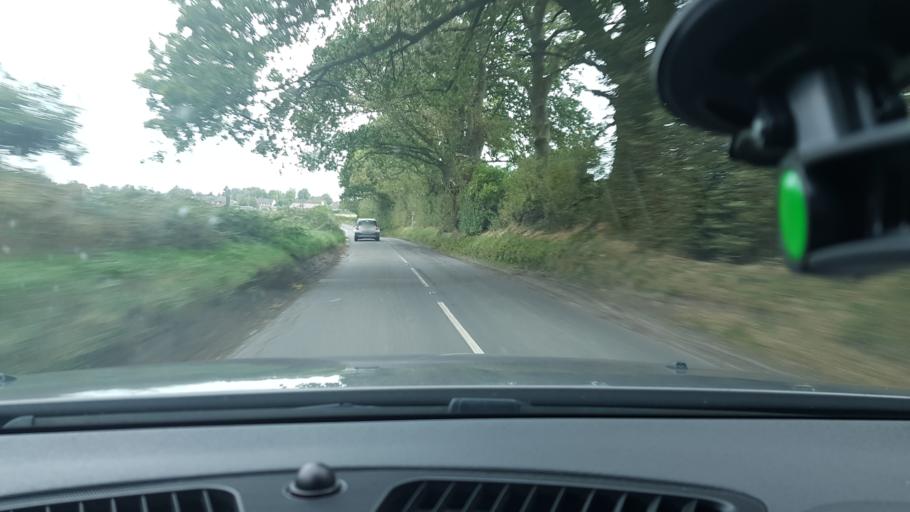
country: GB
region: England
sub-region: Wiltshire
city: Great Bedwyn
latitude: 51.3445
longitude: -1.6197
